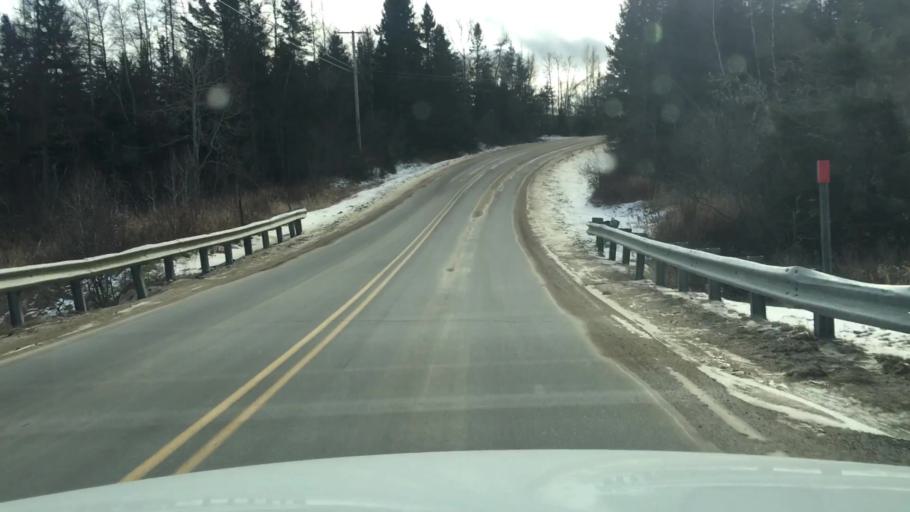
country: US
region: Maine
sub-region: Washington County
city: Jonesport
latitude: 44.6284
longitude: -67.5967
